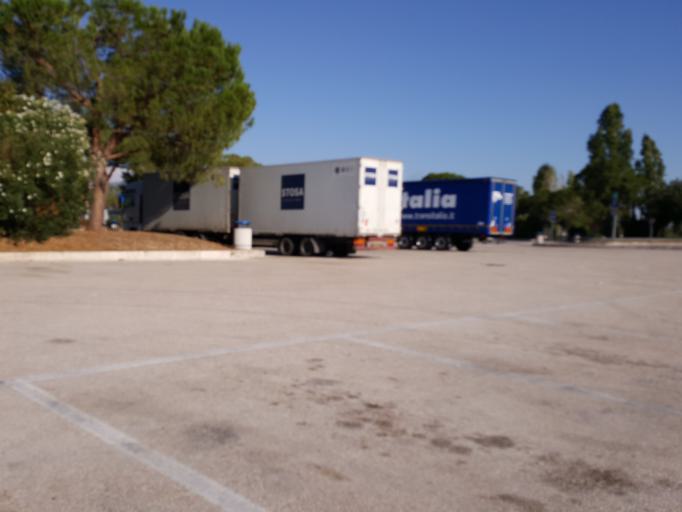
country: IT
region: Latium
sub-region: Citta metropolitana di Roma Capitale
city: Bivio di Capanelle
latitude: 42.1231
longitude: 12.6158
